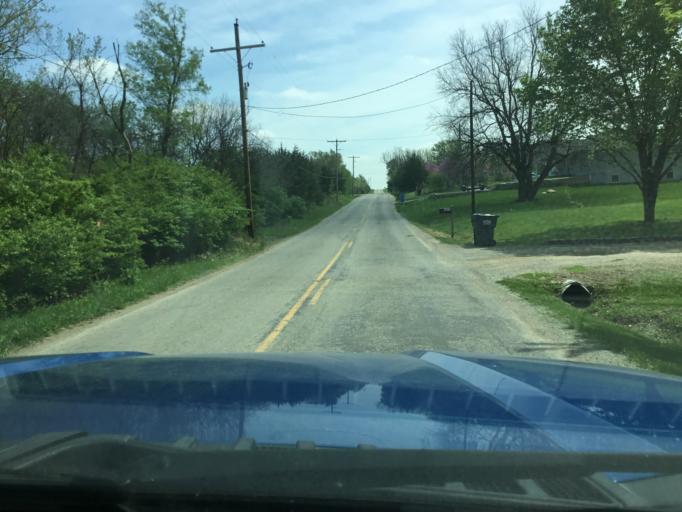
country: US
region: Kansas
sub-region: Shawnee County
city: Topeka
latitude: 39.1170
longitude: -95.5888
